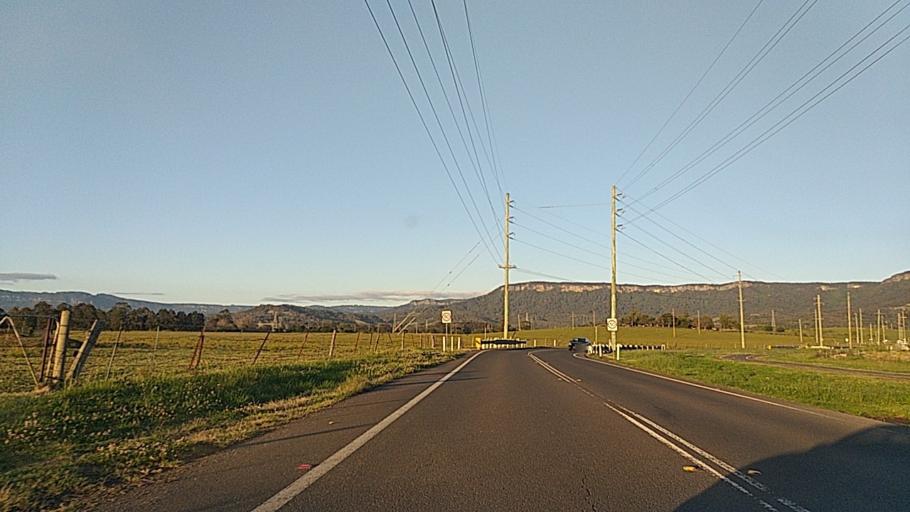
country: AU
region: New South Wales
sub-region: Wollongong
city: Dapto
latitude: -34.5028
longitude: 150.7818
